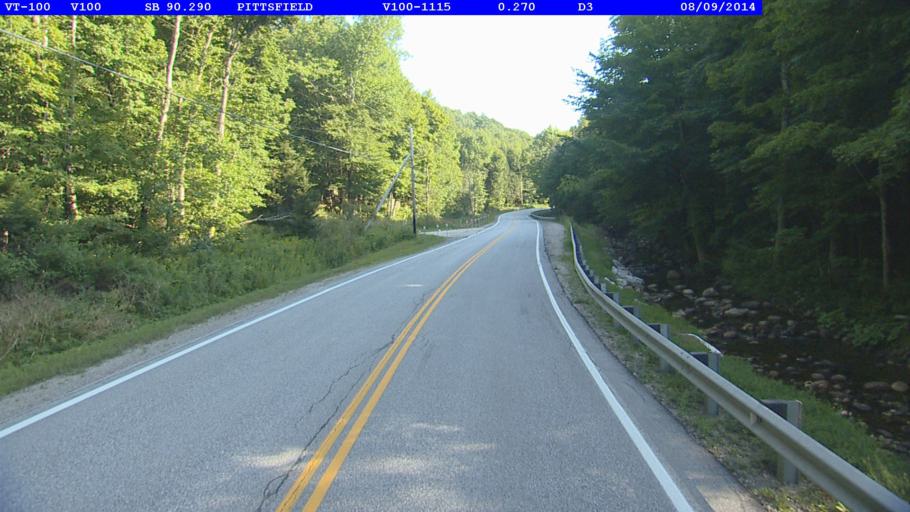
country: US
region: Vermont
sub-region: Rutland County
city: Rutland
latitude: 43.7214
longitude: -72.8228
